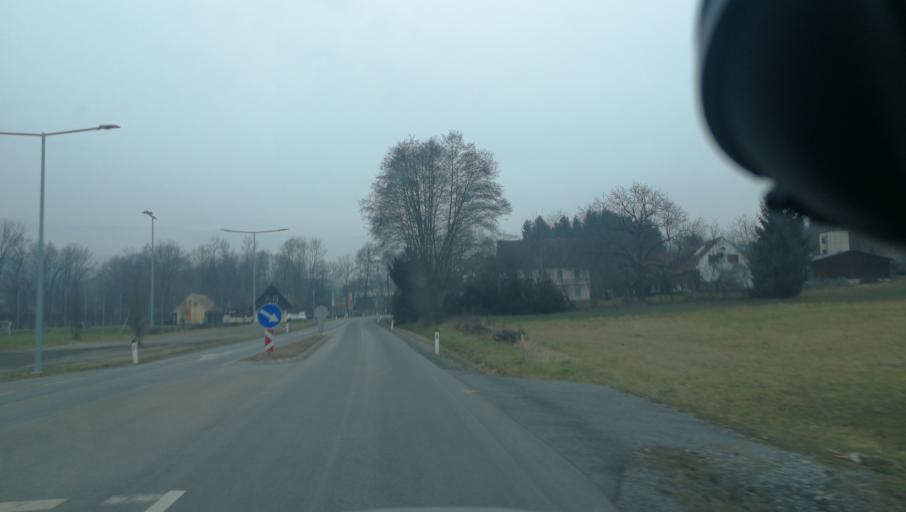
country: AT
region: Styria
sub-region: Politischer Bezirk Deutschlandsberg
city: Stainz
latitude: 46.9004
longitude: 15.2484
